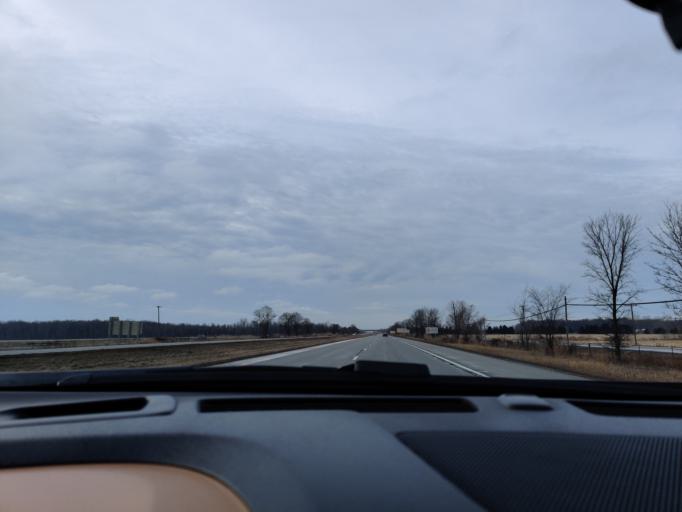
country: CA
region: Quebec
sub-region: Monteregie
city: Les Coteaux
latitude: 45.1811
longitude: -74.3970
